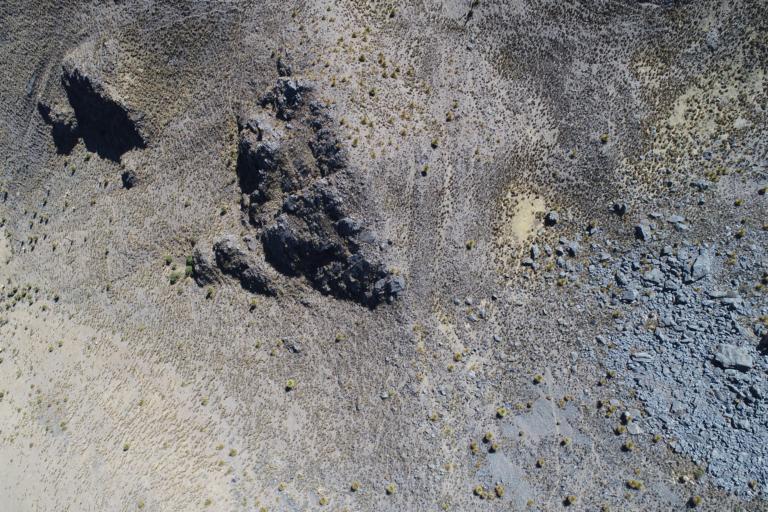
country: BO
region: La Paz
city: Viloco
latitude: -16.8100
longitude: -67.5463
